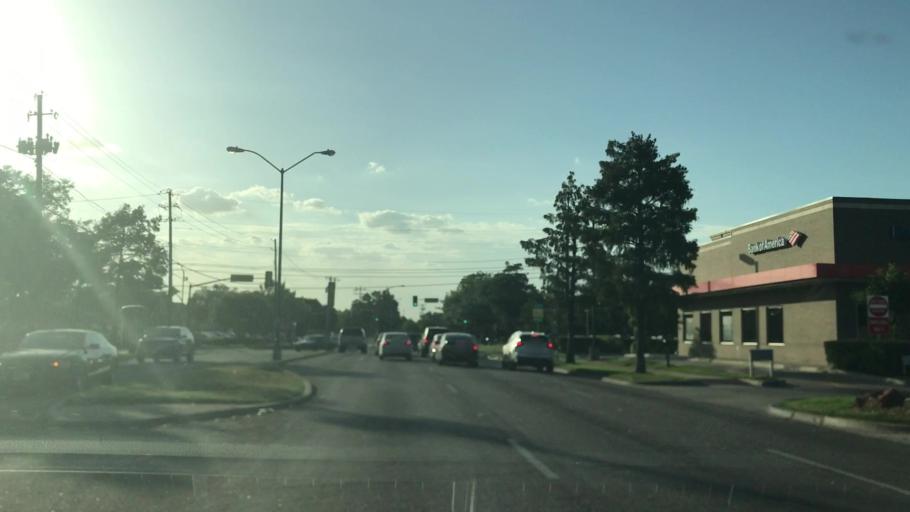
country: US
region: Texas
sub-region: Dallas County
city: University Park
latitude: 32.8293
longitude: -96.8257
